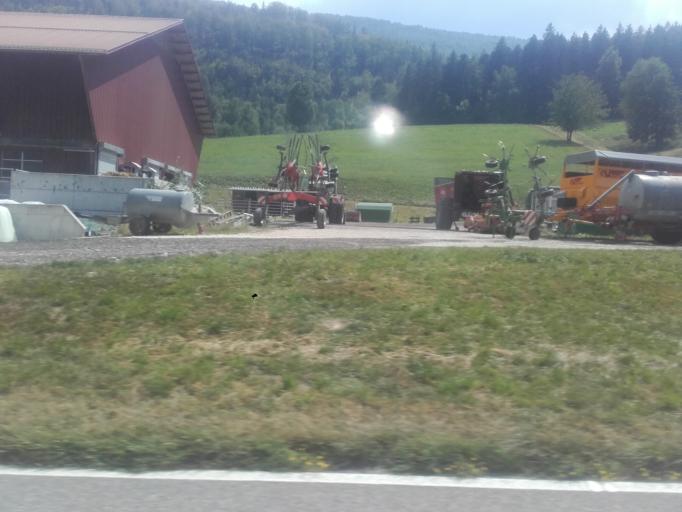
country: CH
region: Solothurn
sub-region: Bezirk Thal
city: Welschenrohr
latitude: 47.2710
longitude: 7.5029
